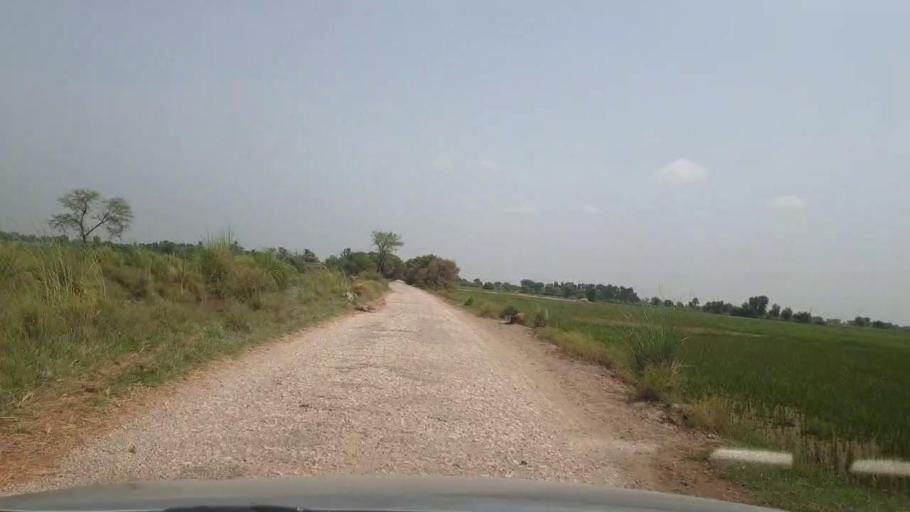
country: PK
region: Sindh
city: Ratodero
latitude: 27.9315
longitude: 68.3633
